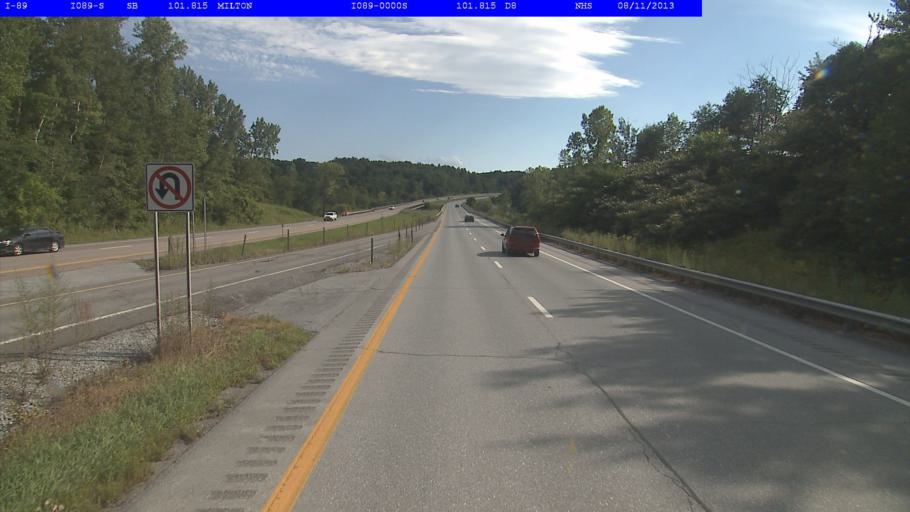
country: US
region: Vermont
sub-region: Chittenden County
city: Milton
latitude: 44.6393
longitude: -73.1402
